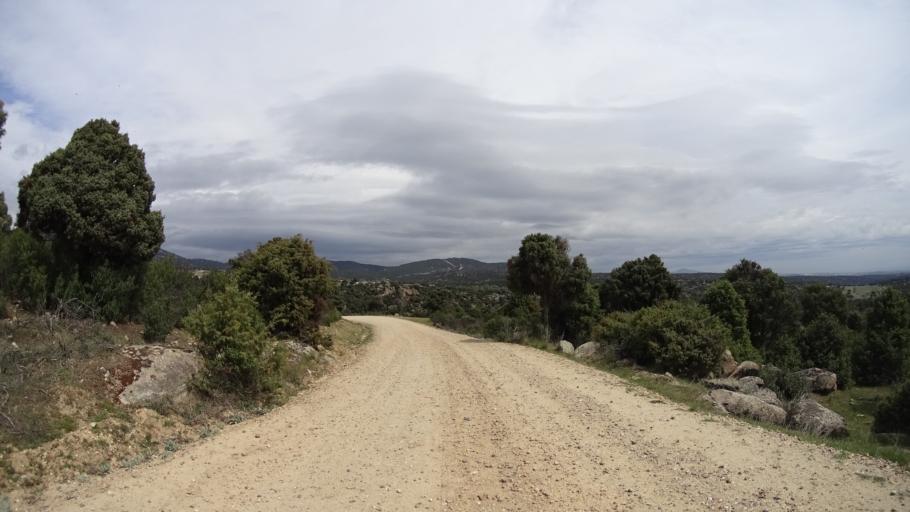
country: ES
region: Madrid
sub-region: Provincia de Madrid
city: Hoyo de Manzanares
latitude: 40.6173
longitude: -3.8770
